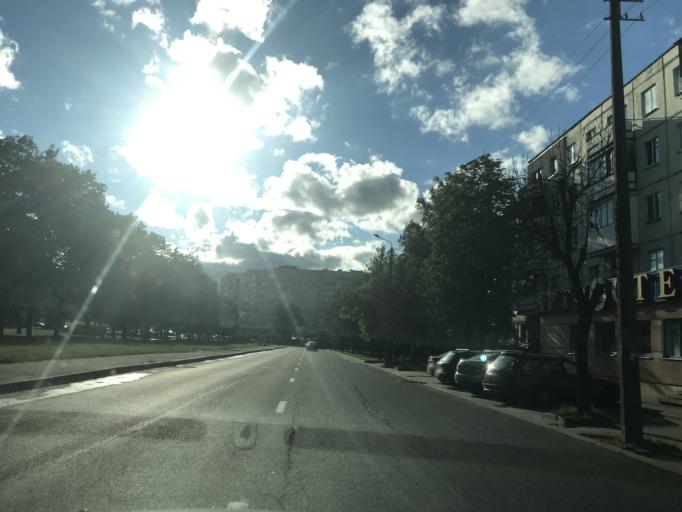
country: BY
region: Minsk
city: Minsk
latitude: 53.9493
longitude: 27.6190
